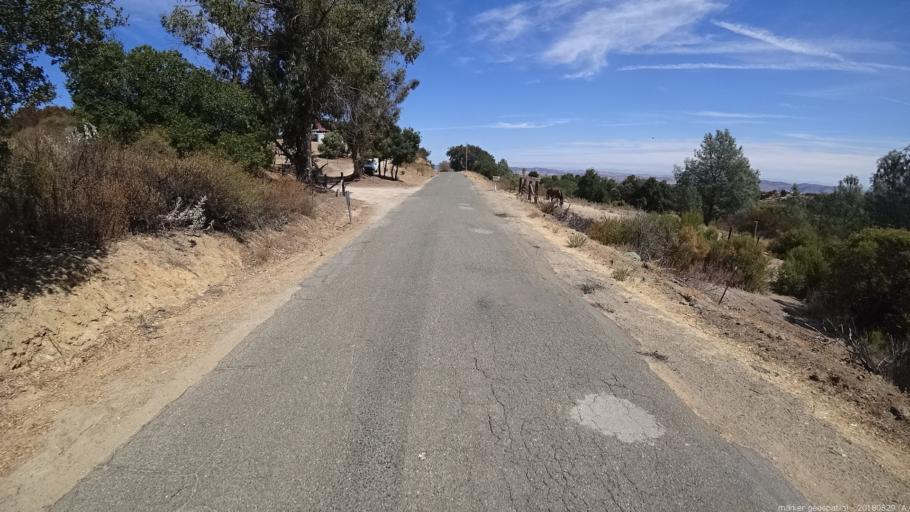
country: US
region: California
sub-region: San Luis Obispo County
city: Lake Nacimiento
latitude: 35.8202
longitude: -121.0573
